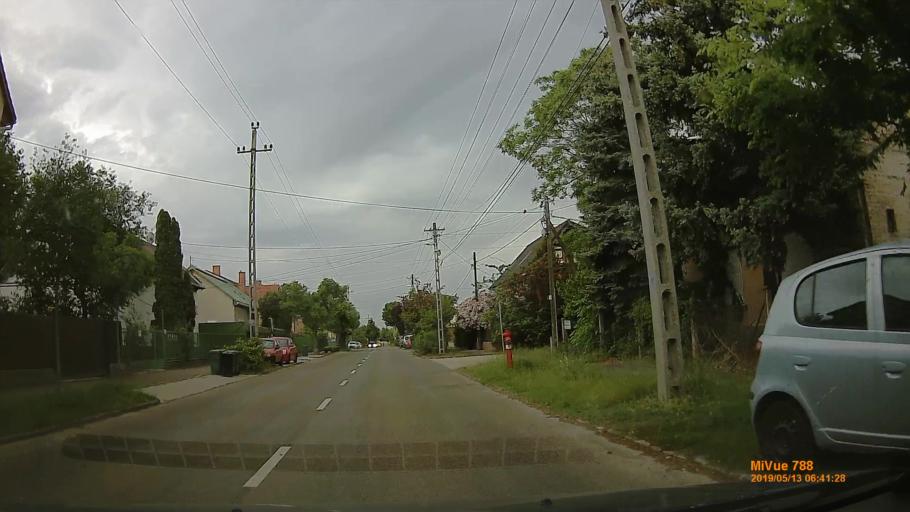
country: HU
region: Budapest
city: Budapest XXI. keruelet
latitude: 47.4196
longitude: 19.0888
